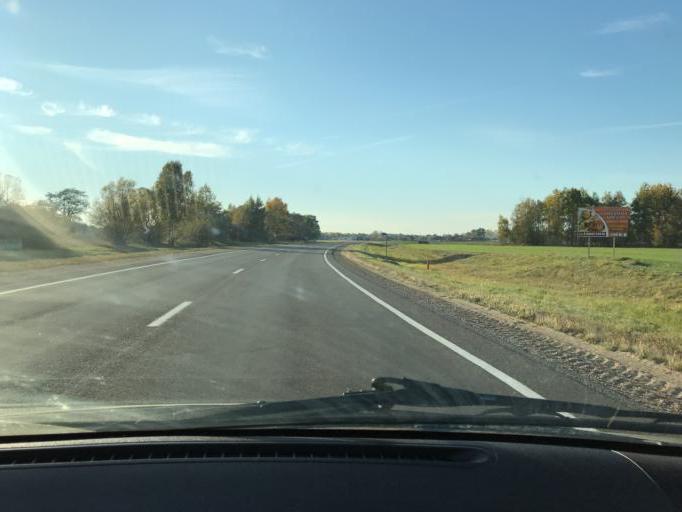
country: BY
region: Brest
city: Horad Kobryn
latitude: 52.2073
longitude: 24.5743
